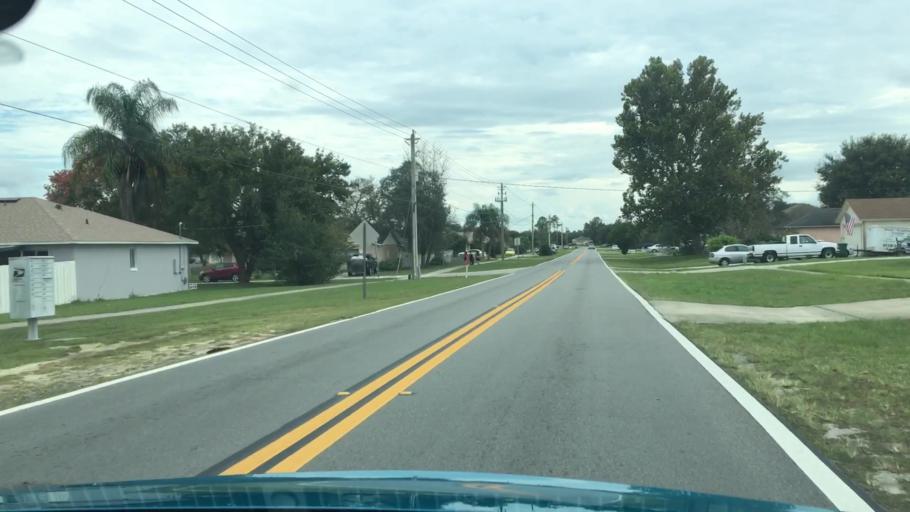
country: US
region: Florida
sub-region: Volusia County
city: Lake Helen
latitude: 28.9403
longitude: -81.1807
